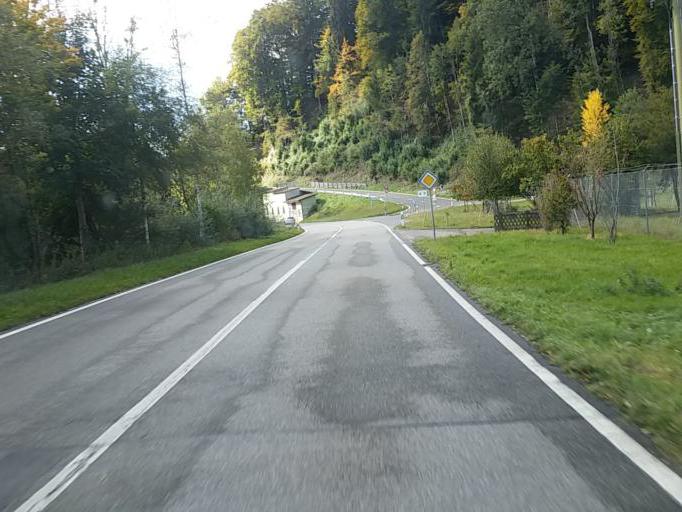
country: CH
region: Bern
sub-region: Emmental District
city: Trachselwald
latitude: 47.0166
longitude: 7.7251
